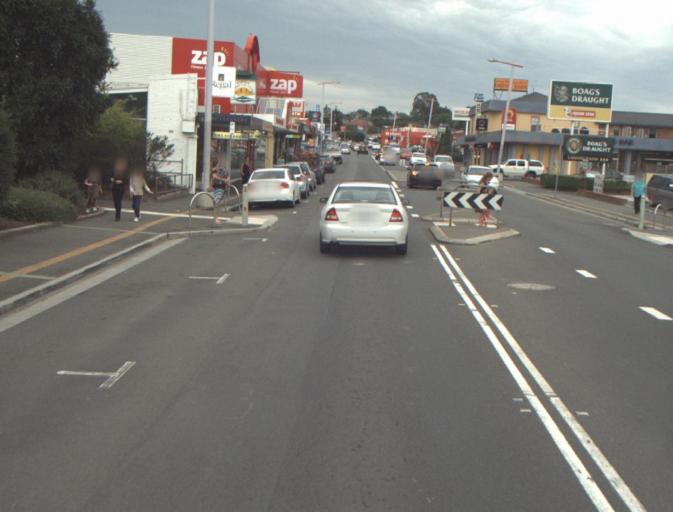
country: AU
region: Tasmania
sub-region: Launceston
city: East Launceston
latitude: -41.4667
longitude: 147.1599
